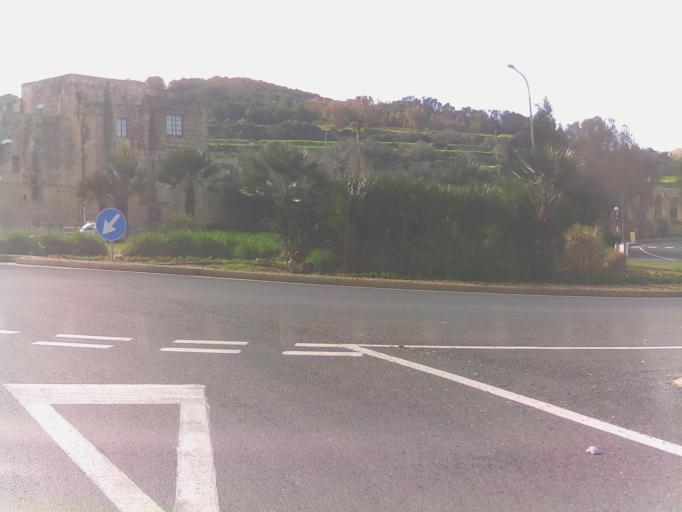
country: MT
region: Il-Mellieha
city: Mellieha
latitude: 35.9442
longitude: 14.3845
